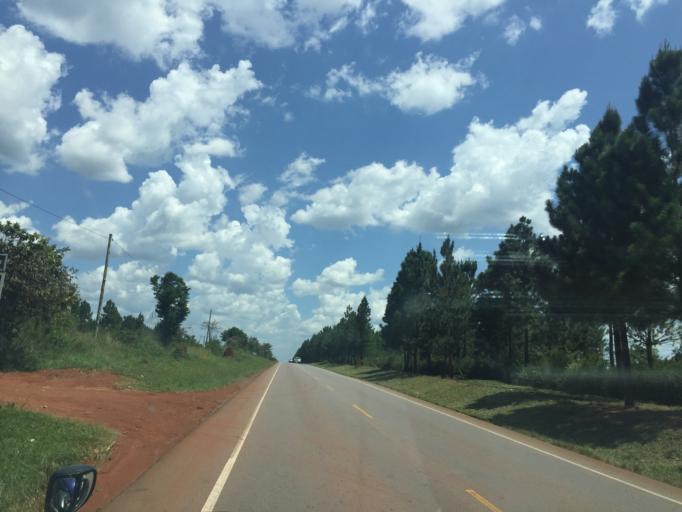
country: UG
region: Central Region
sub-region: Nakasongola District
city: Nakasongola
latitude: 1.3777
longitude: 32.3430
